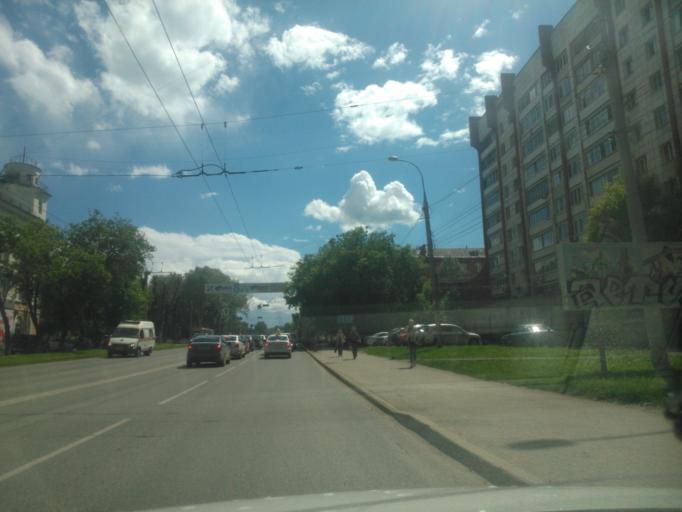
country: RU
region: Perm
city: Perm
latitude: 57.9889
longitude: 56.2485
